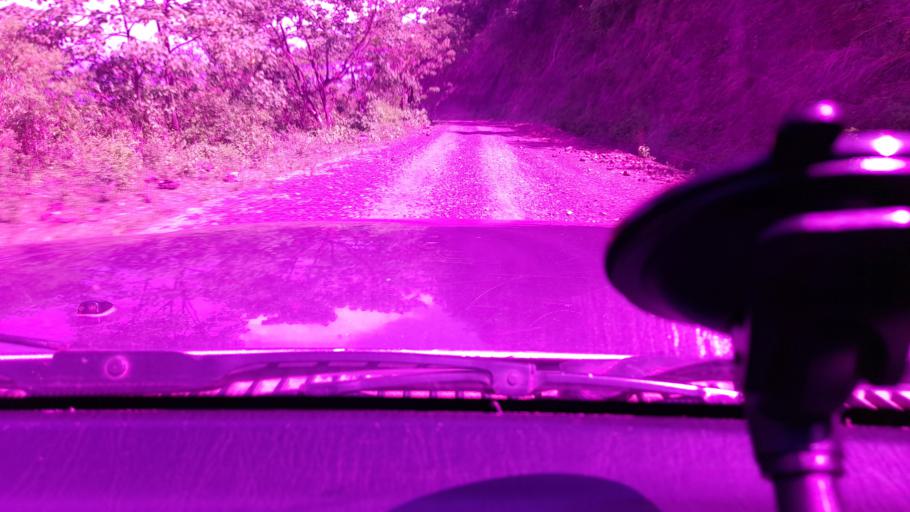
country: ET
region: Oromiya
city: Jima
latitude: 7.8246
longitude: 37.5429
